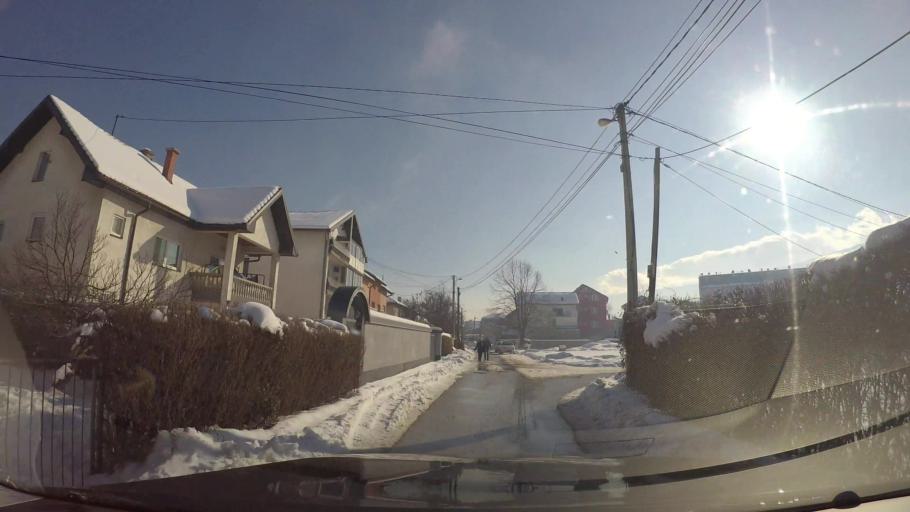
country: BA
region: Federation of Bosnia and Herzegovina
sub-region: Kanton Sarajevo
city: Sarajevo
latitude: 43.8123
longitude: 18.3133
